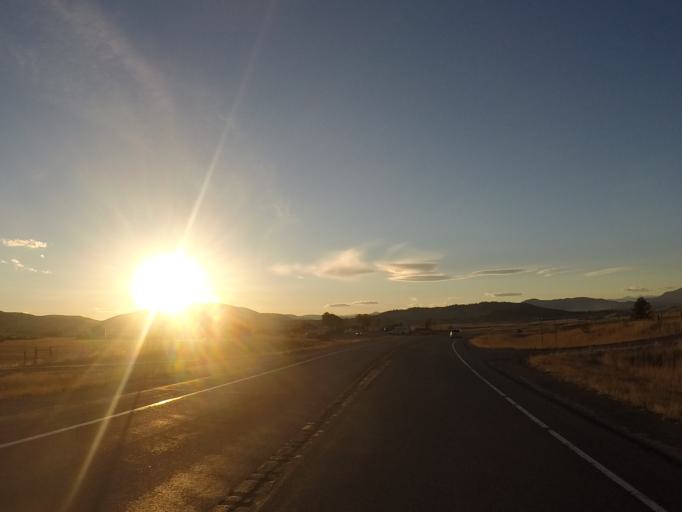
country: US
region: Montana
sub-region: Missoula County
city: Seeley Lake
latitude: 47.0201
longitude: -113.1198
